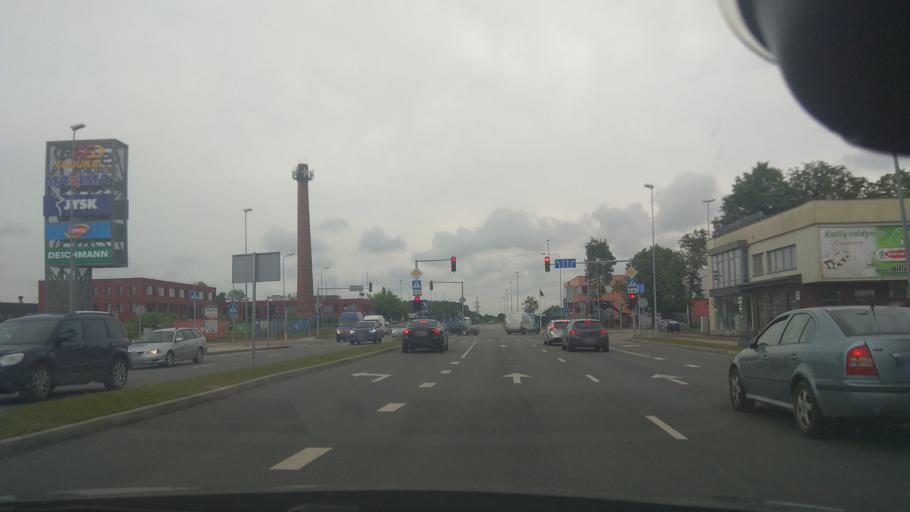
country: LT
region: Klaipedos apskritis
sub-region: Klaipeda
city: Klaipeda
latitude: 55.7232
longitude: 21.1573
